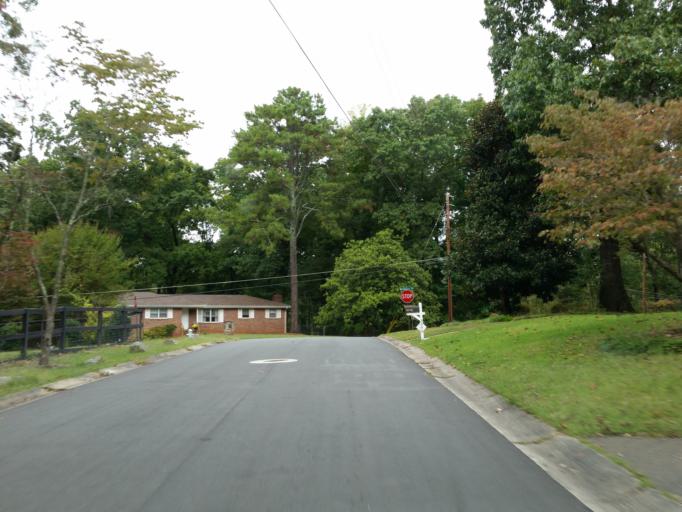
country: US
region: Georgia
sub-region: Cherokee County
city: Woodstock
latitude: 34.0321
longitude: -84.5122
